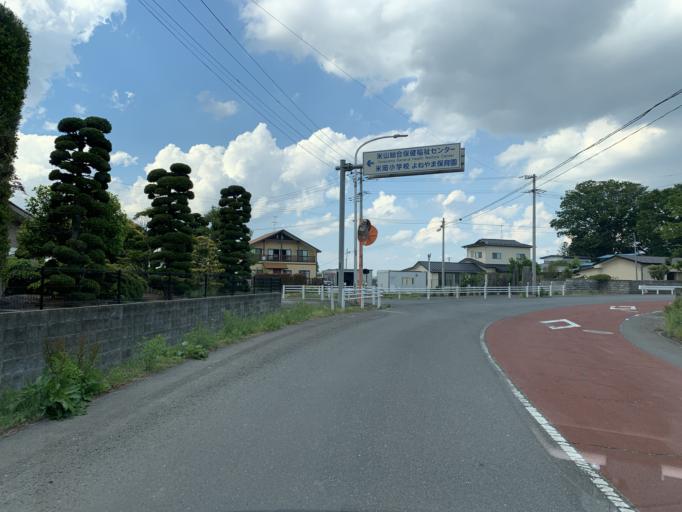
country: JP
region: Miyagi
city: Wakuya
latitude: 38.6331
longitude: 141.2026
